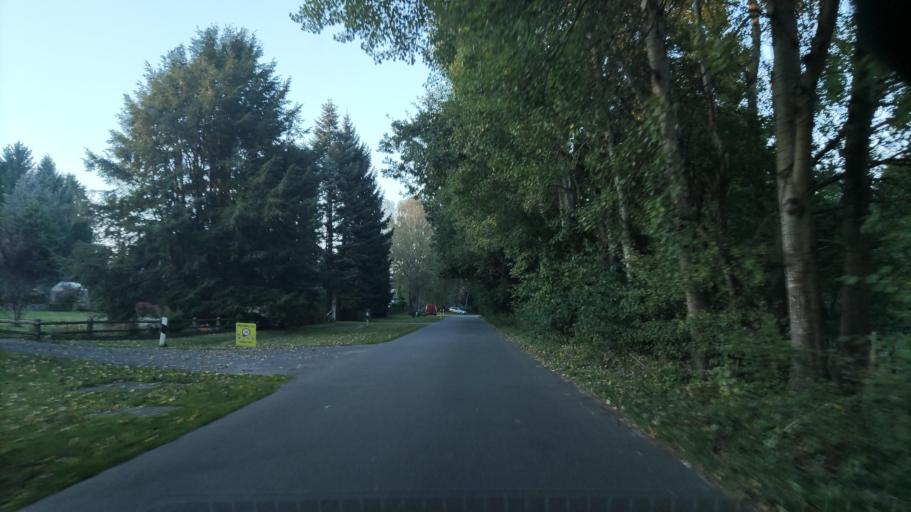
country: DE
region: Lower Saxony
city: Bispingen
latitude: 53.0887
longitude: 10.0196
